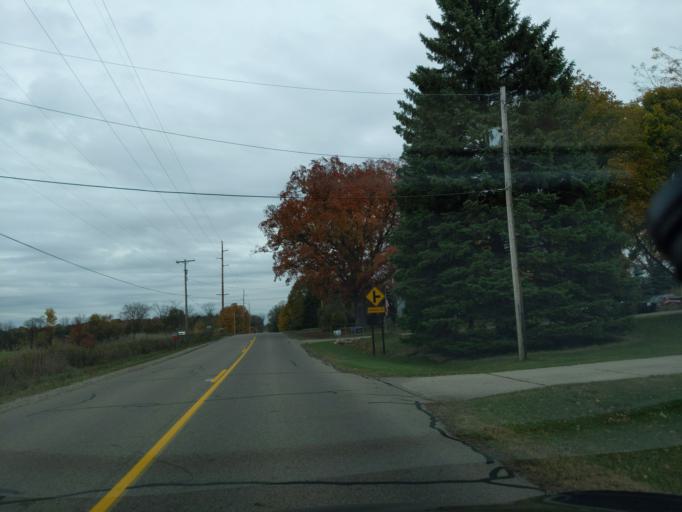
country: US
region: Michigan
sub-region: Eaton County
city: Eaton Rapids
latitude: 42.5239
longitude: -84.6342
